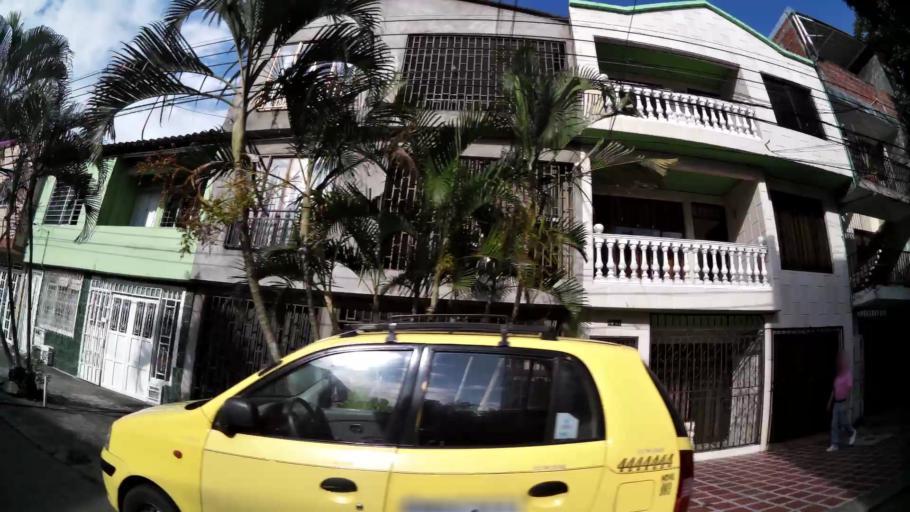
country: CO
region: Valle del Cauca
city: Cali
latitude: 3.4311
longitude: -76.5262
